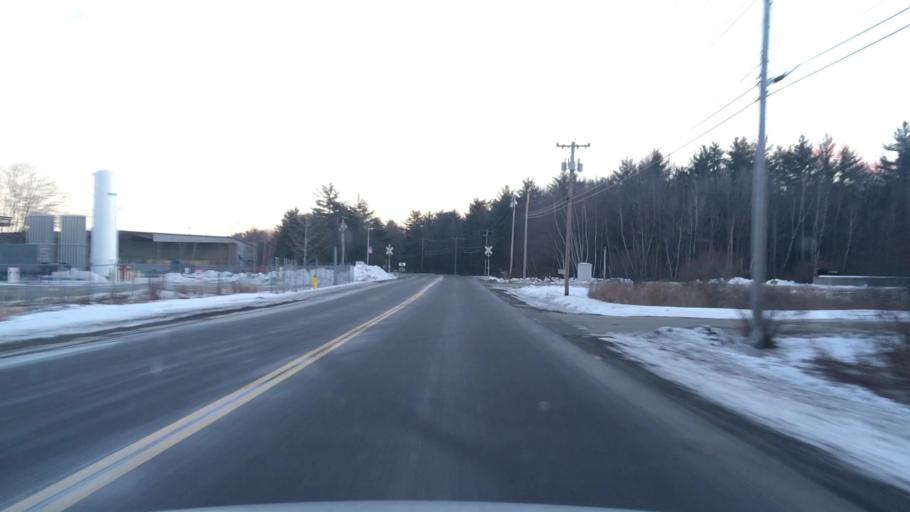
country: US
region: Maine
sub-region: Androscoggin County
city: Auburn
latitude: 44.0729
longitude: -70.2539
